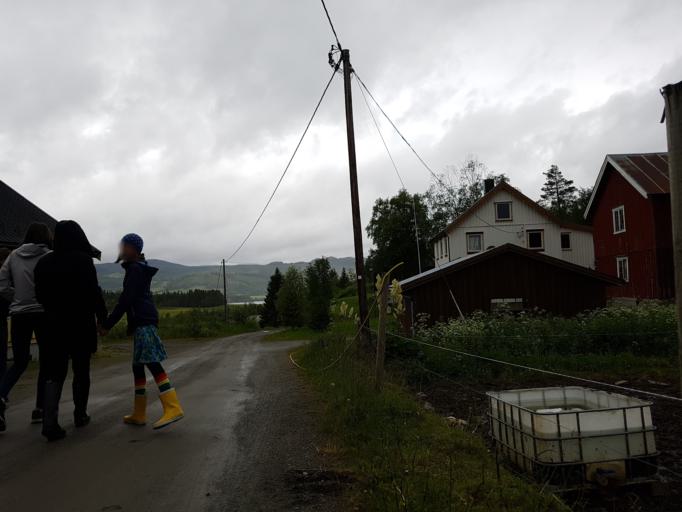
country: NO
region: Sor-Trondelag
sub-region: Selbu
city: Mebonden
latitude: 63.2597
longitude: 11.0861
